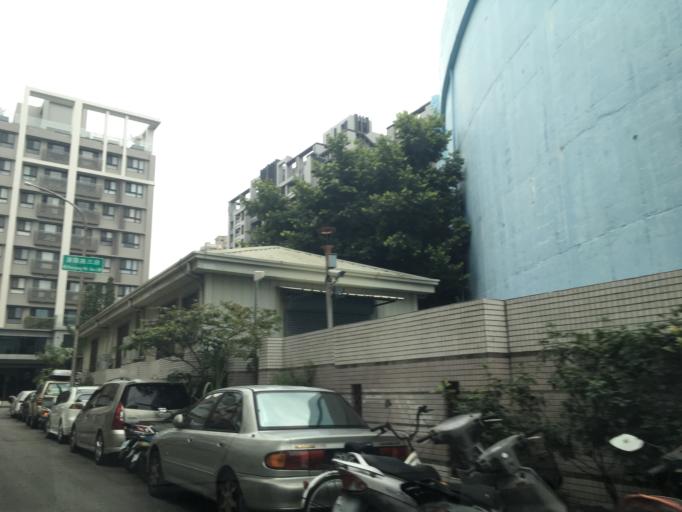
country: TW
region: Taiwan
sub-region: Taichung City
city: Taichung
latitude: 24.1716
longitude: 120.6962
